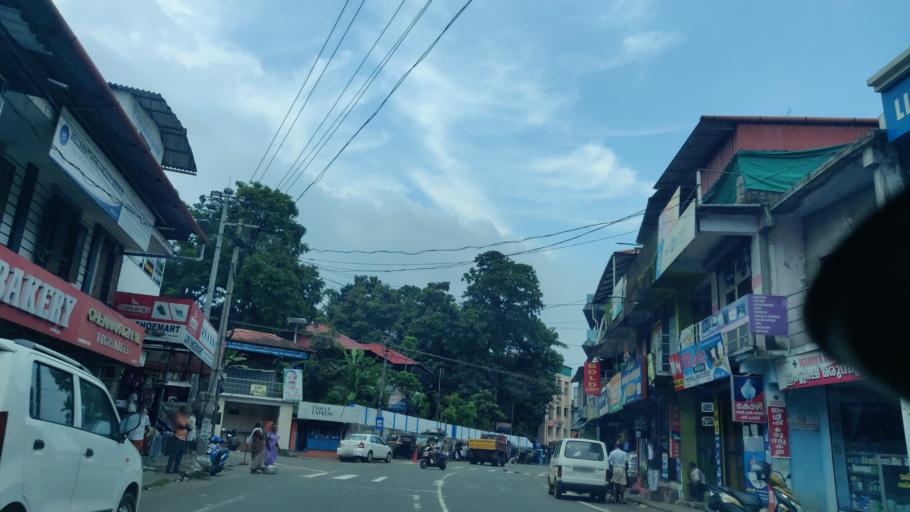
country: IN
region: Kerala
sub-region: Kottayam
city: Palackattumala
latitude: 9.8525
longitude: 76.6867
